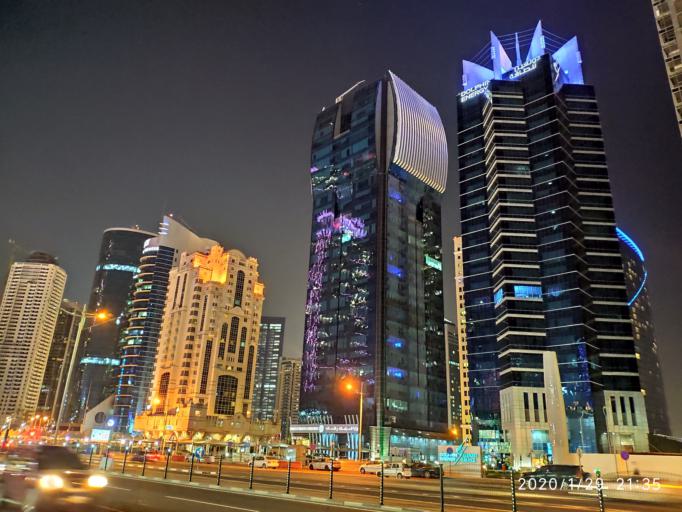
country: QA
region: Baladiyat ad Dawhah
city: Doha
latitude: 25.3260
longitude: 51.5310
